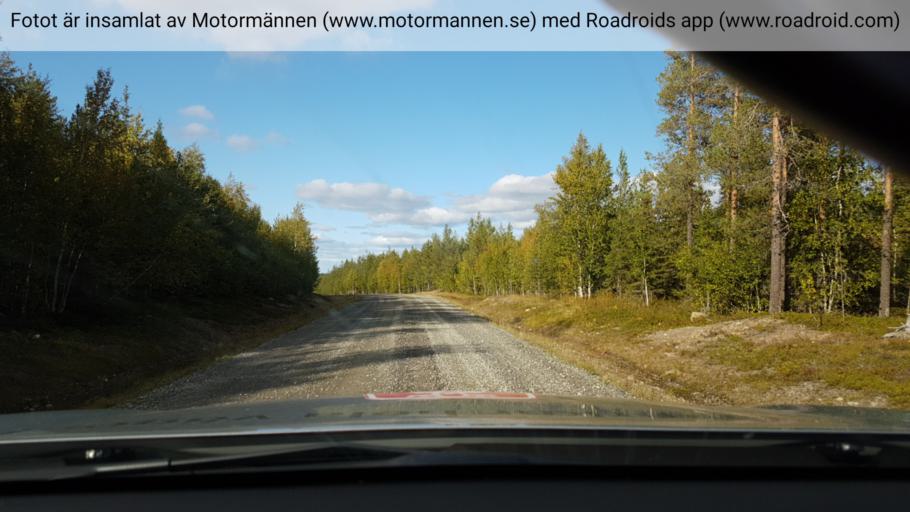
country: SE
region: Vaesterbotten
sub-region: Sorsele Kommun
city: Sorsele
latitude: 65.4189
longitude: 18.1071
